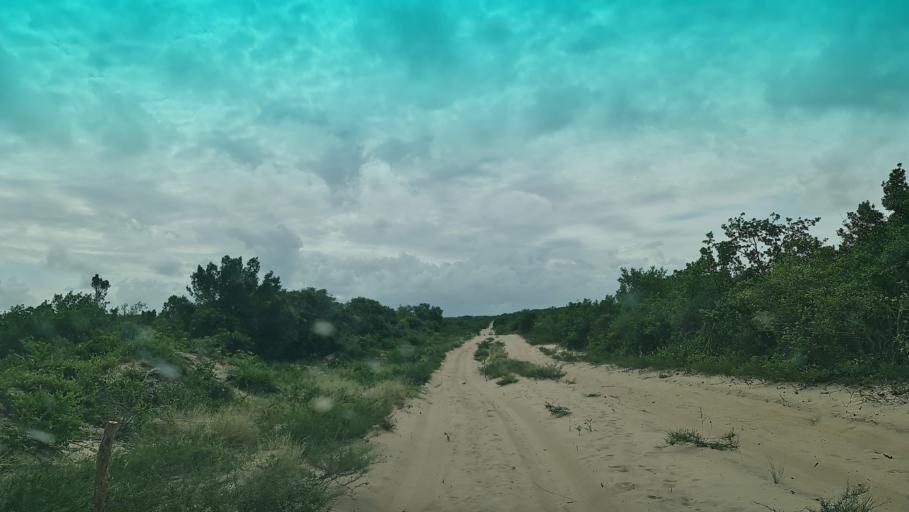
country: MZ
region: Maputo
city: Manhica
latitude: -25.4390
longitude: 32.9238
